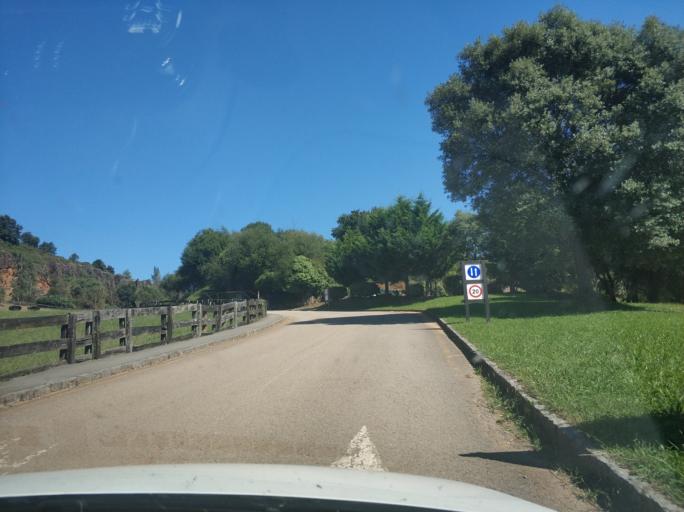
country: ES
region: Cantabria
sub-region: Provincia de Cantabria
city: Penagos
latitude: 43.3572
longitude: -3.8340
